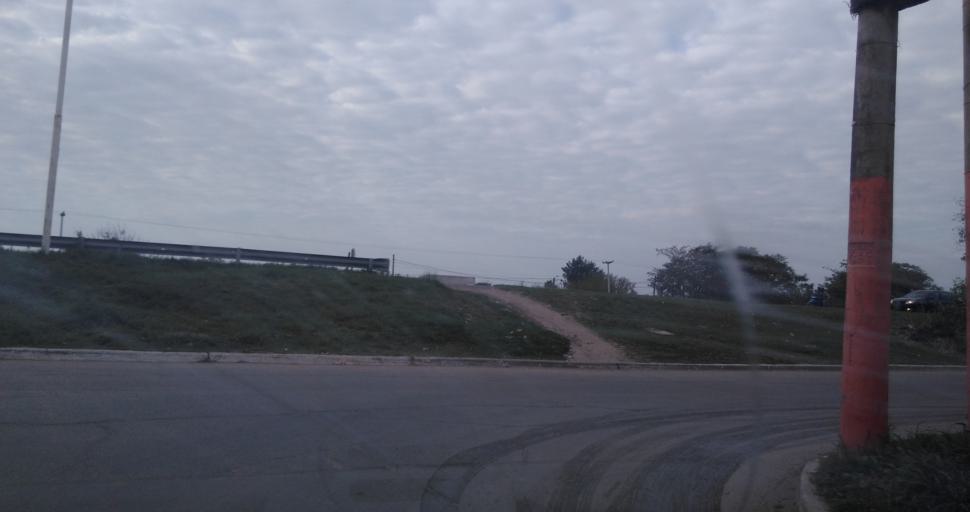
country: AR
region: Chaco
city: Fontana
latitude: -27.4542
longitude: -59.0331
